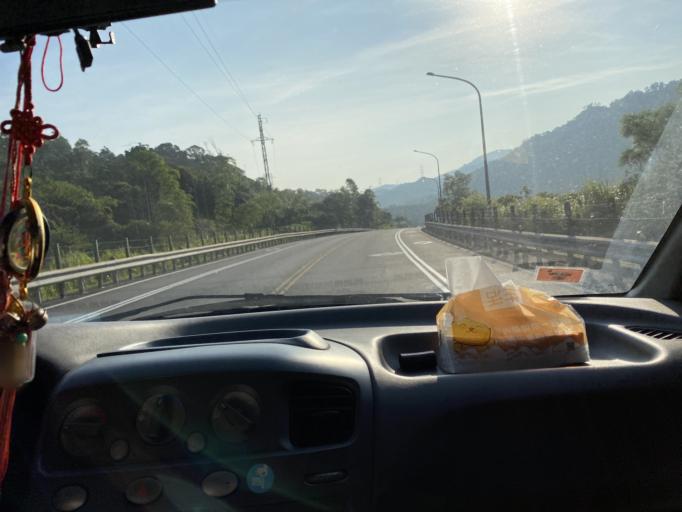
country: TW
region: Taiwan
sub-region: Keelung
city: Keelung
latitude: 25.0209
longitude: 121.8095
